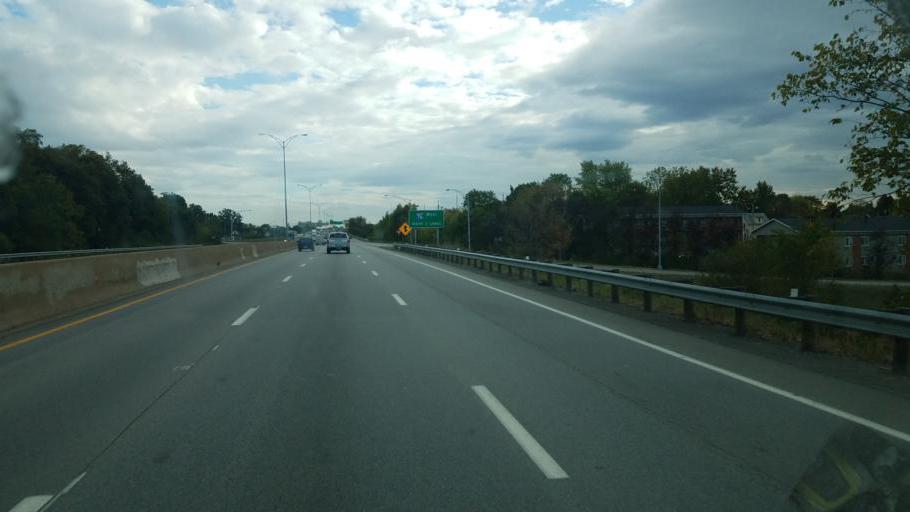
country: US
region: Ohio
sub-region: Summit County
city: Barberton
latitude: 41.0461
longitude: -81.5651
